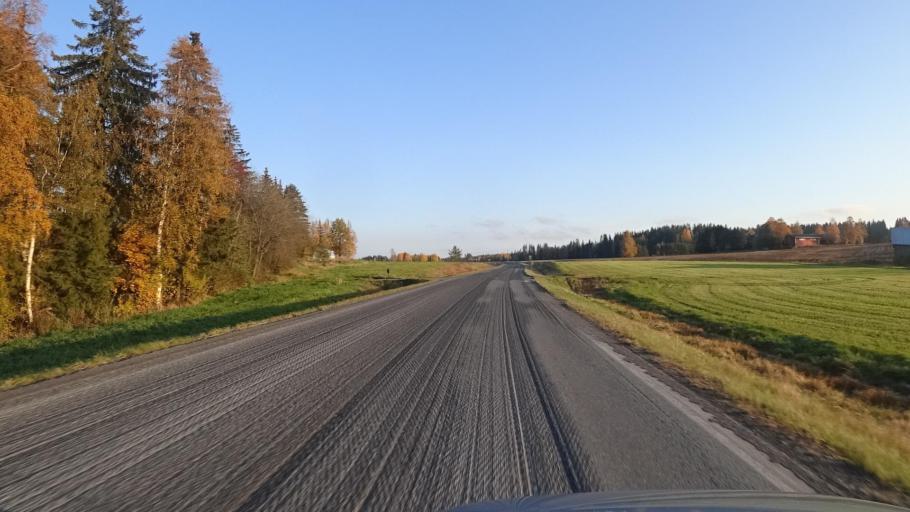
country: FI
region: Haeme
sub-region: Forssa
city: Ypaejae
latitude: 60.7832
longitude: 23.3058
